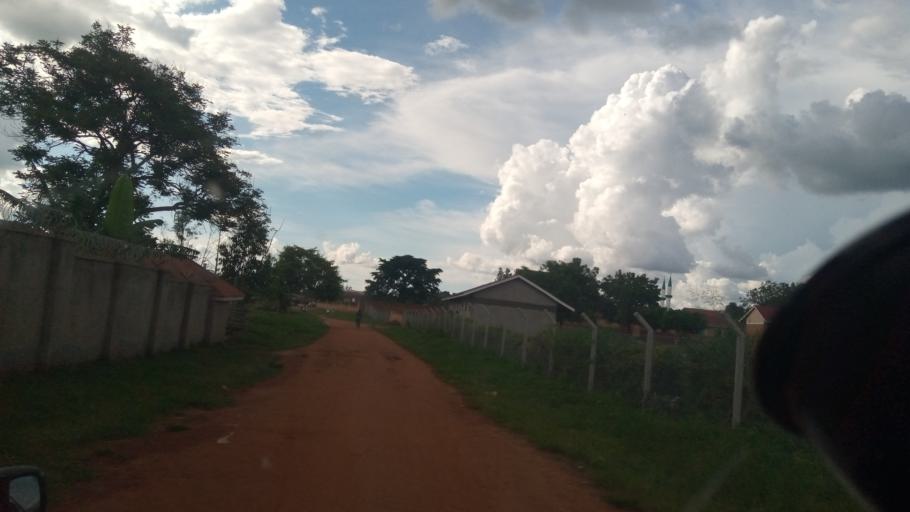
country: UG
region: Northern Region
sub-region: Lira District
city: Lira
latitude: 2.2413
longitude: 32.9005
